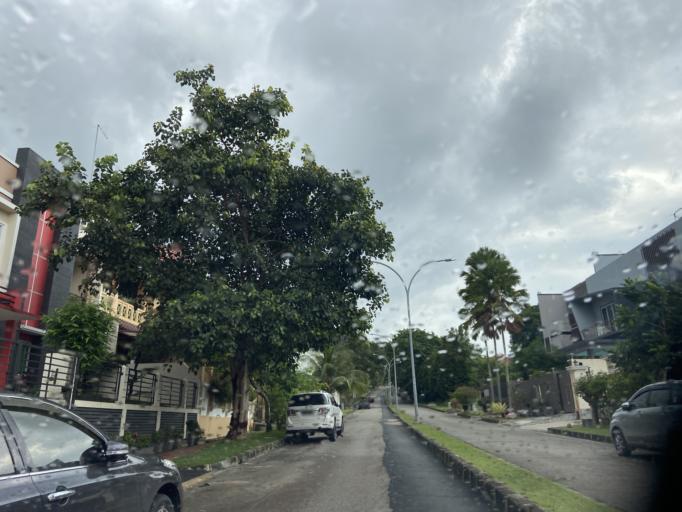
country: SG
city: Singapore
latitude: 1.1070
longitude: 104.0244
